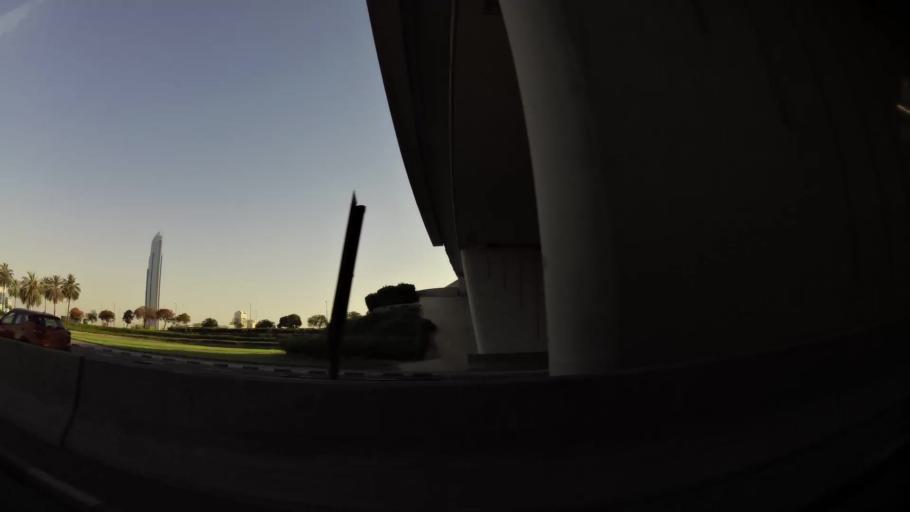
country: AE
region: Ash Shariqah
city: Sharjah
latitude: 25.2380
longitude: 55.3439
